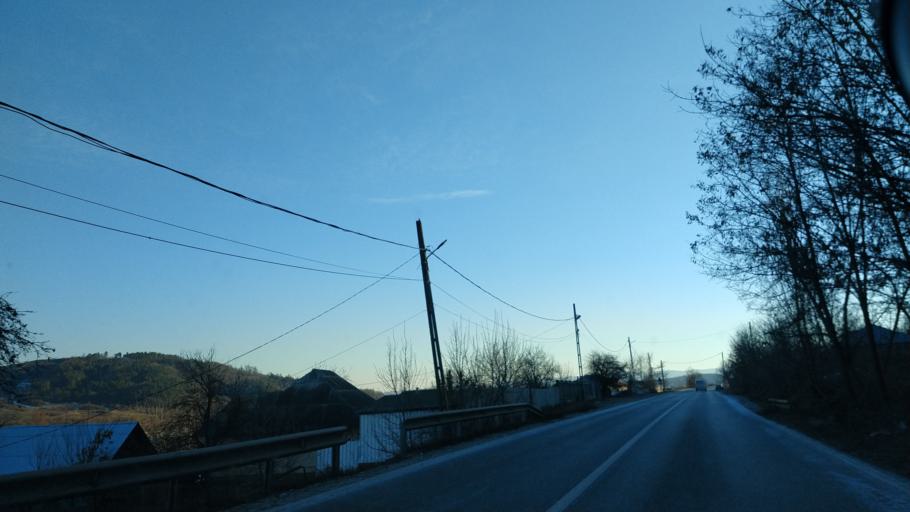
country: RO
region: Bacau
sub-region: Comuna Helegiu
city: Bratila
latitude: 46.3032
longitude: 26.7528
